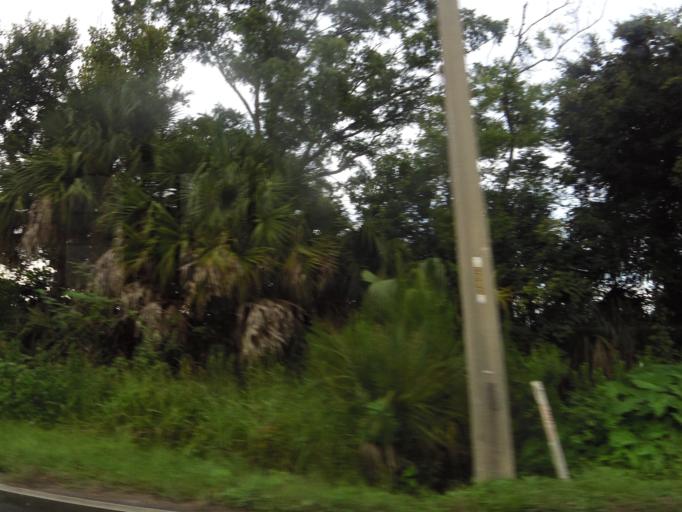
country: US
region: Florida
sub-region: Duval County
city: Jacksonville
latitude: 30.3573
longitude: -81.7181
